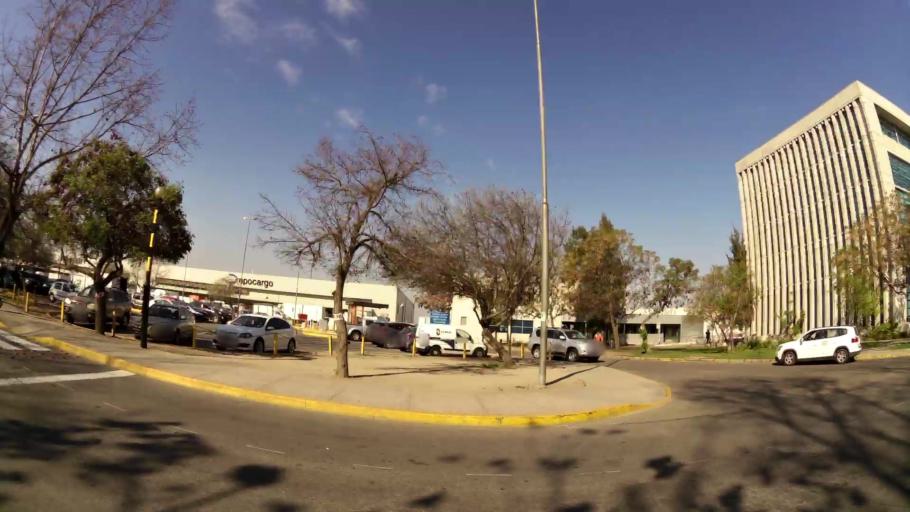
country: CL
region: Santiago Metropolitan
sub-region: Provincia de Santiago
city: Lo Prado
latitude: -33.4046
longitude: -70.7918
